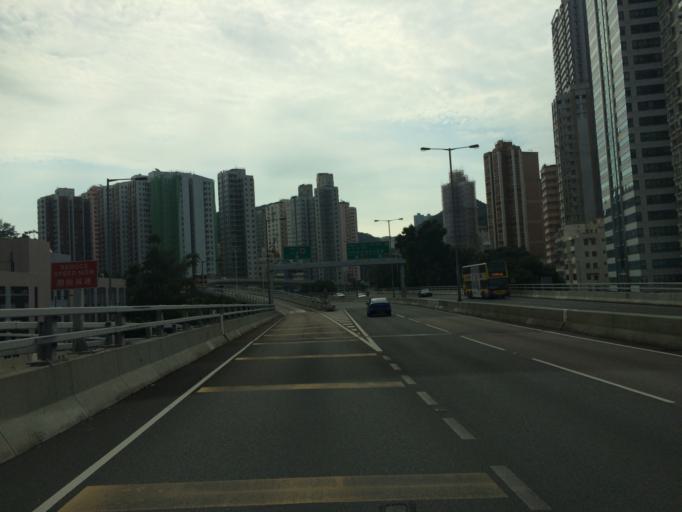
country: HK
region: Wanchai
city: Wan Chai
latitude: 22.2804
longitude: 114.2262
